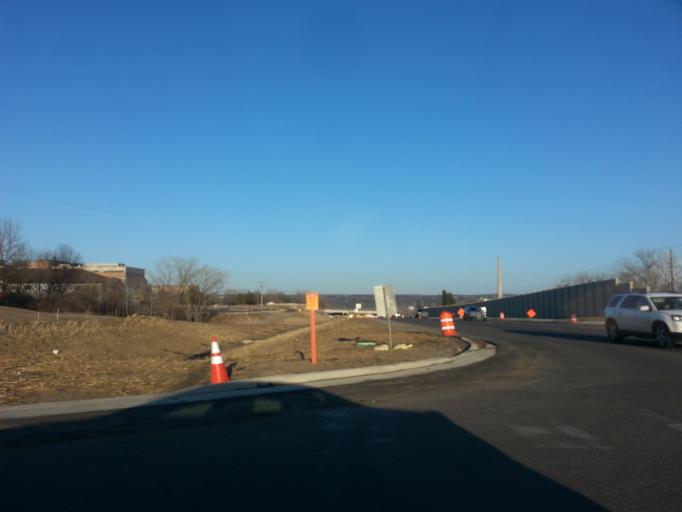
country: US
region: Minnesota
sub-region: Washington County
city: Oak Park Heights
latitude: 45.0352
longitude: -92.8074
